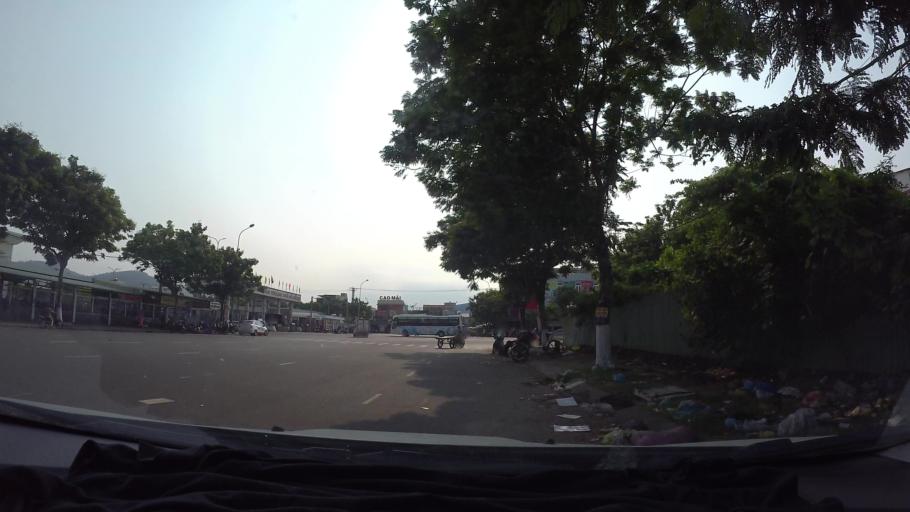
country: VN
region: Da Nang
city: Lien Chieu
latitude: 16.0569
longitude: 108.1730
